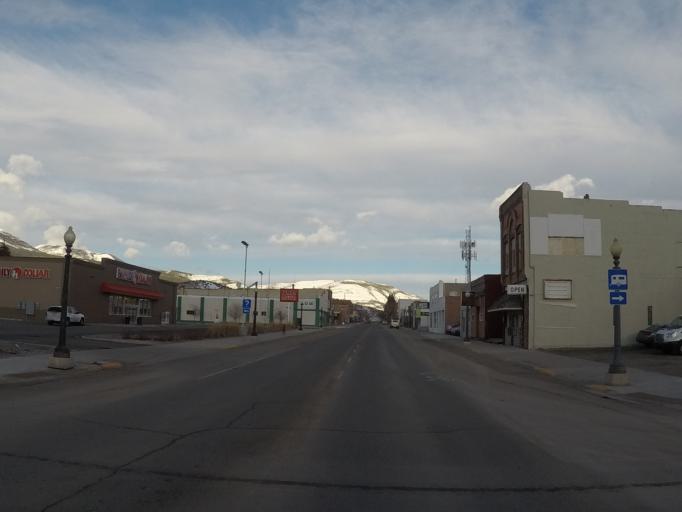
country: US
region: Montana
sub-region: Deer Lodge County
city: Anaconda
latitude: 46.1296
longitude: -112.9483
